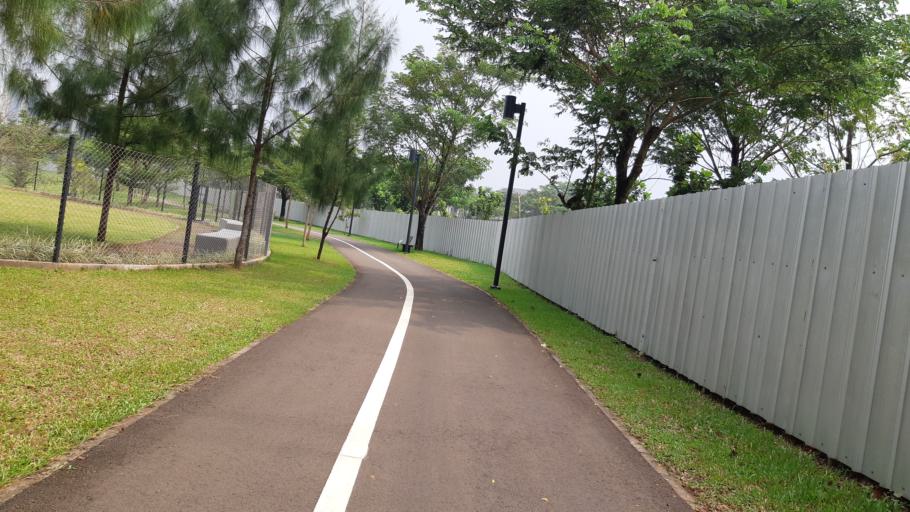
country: ID
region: West Java
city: Serpong
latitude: -6.2937
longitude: 106.6521
